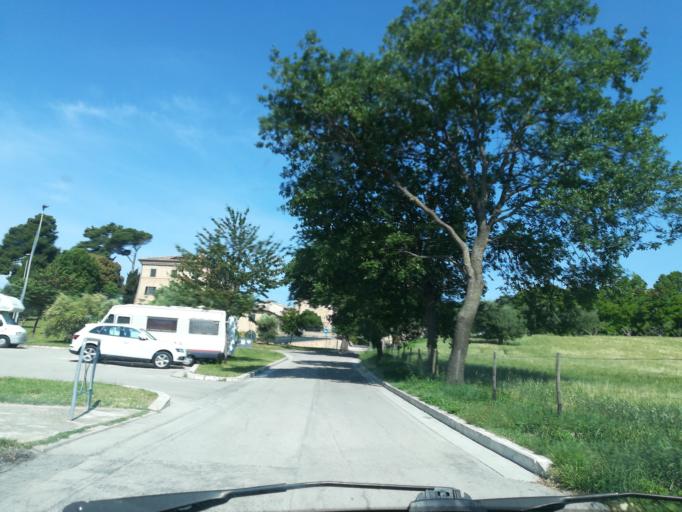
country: IT
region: The Marches
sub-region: Provincia di Macerata
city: Piediripa
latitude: 43.2923
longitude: 13.4731
